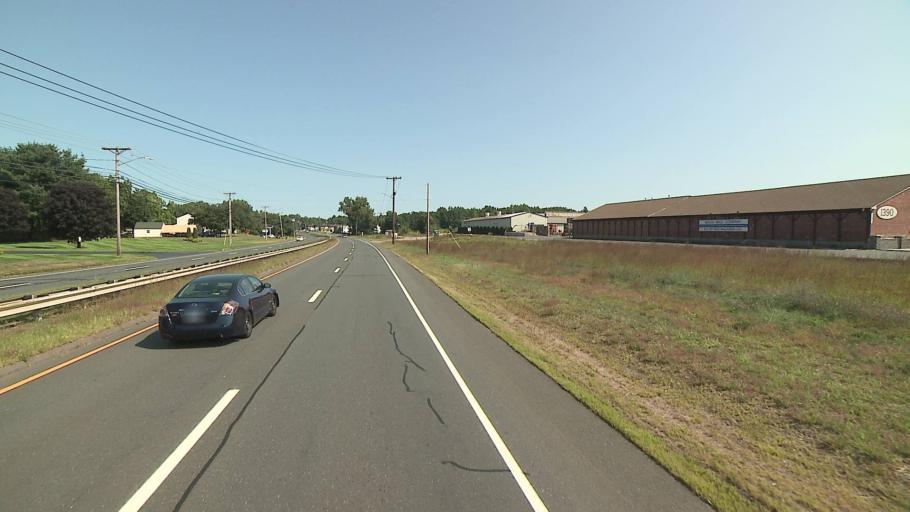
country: US
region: Connecticut
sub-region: Hartford County
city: South Windsor
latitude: 41.8439
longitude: -72.6001
